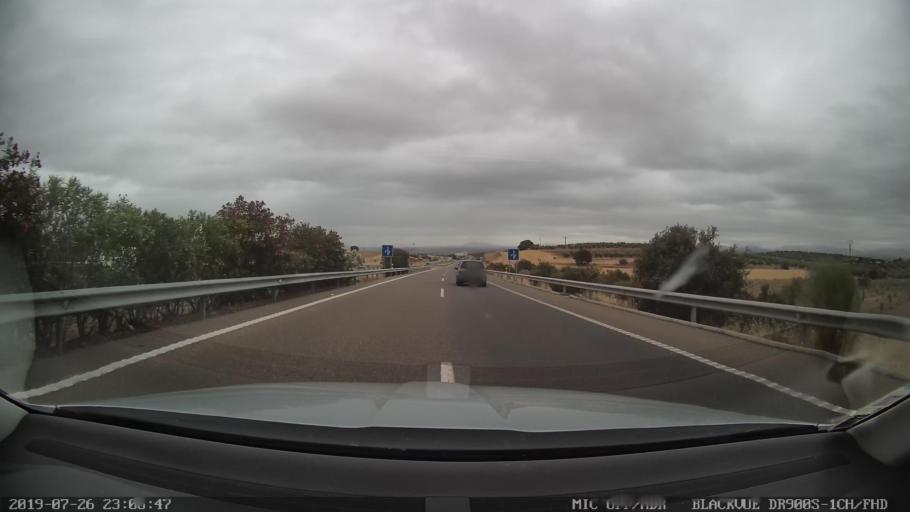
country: ES
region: Extremadura
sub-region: Provincia de Badajoz
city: San Pedro de Merida
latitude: 38.9493
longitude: -6.1985
